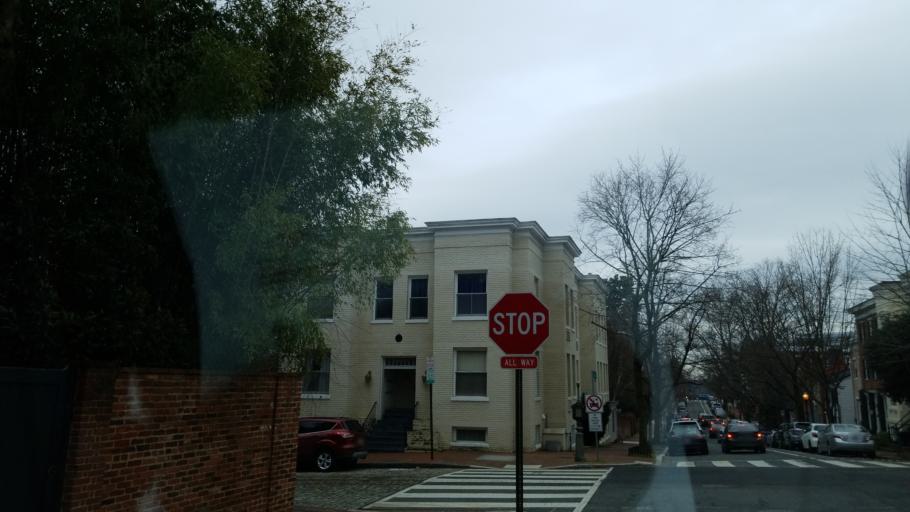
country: US
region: Washington, D.C.
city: Washington, D.C.
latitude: 38.9079
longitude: -77.0678
